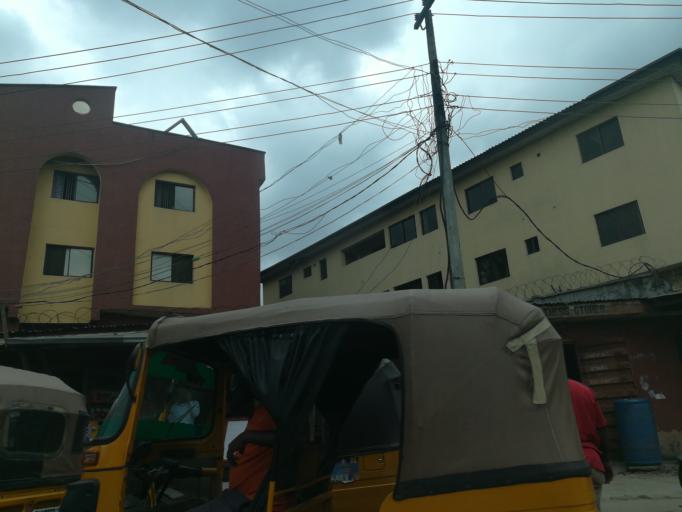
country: NG
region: Lagos
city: Ojota
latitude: 6.6072
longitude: 3.3996
